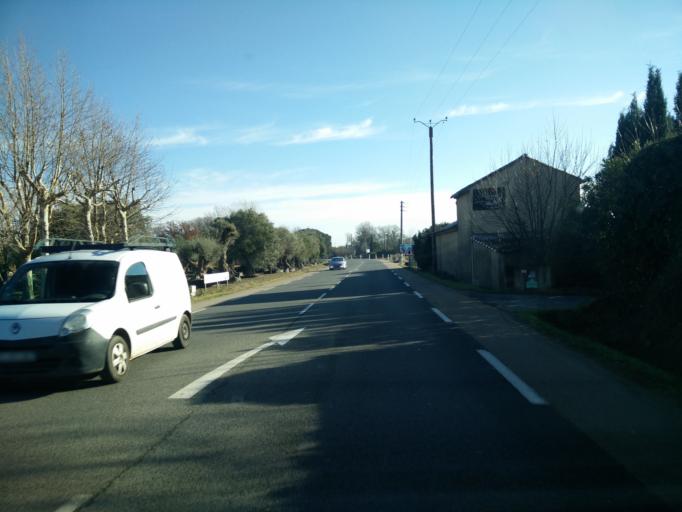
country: FR
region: Provence-Alpes-Cote d'Azur
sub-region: Departement du Var
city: Grimaud
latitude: 43.2692
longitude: 6.5454
